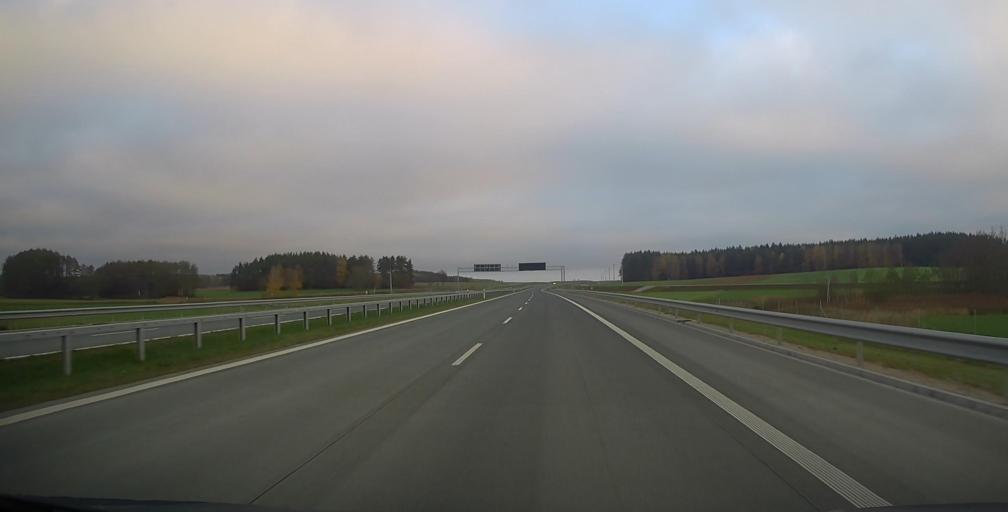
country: PL
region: Podlasie
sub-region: Powiat kolnenski
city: Stawiski
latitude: 53.4668
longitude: 22.2048
